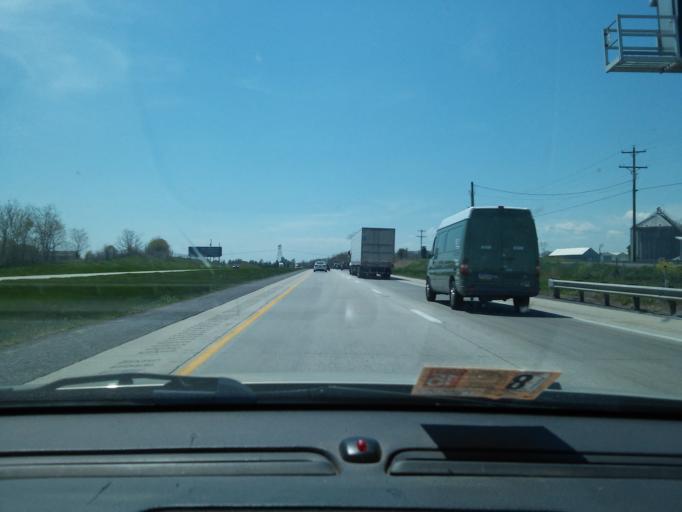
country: US
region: Pennsylvania
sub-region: Cumberland County
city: Shippensburg
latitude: 40.0105
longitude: -77.5406
